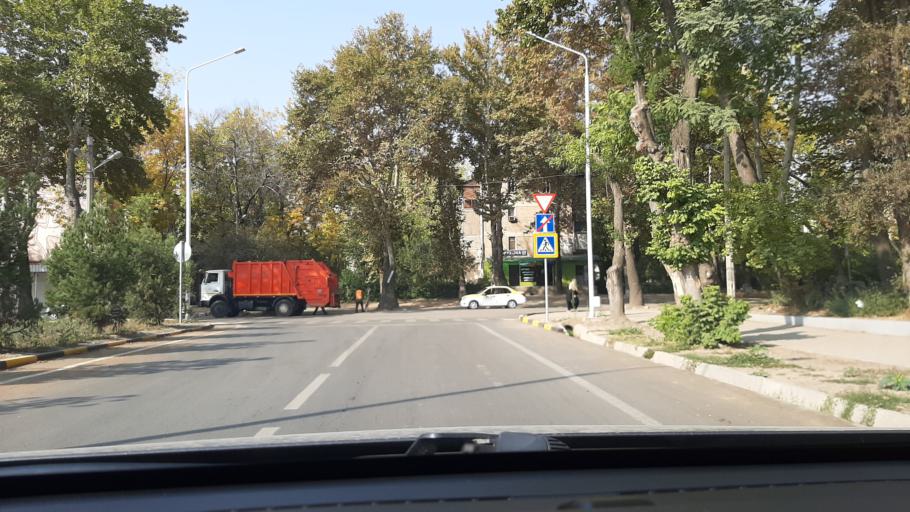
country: TJ
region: Dushanbe
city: Dushanbe
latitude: 38.5640
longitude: 68.7487
